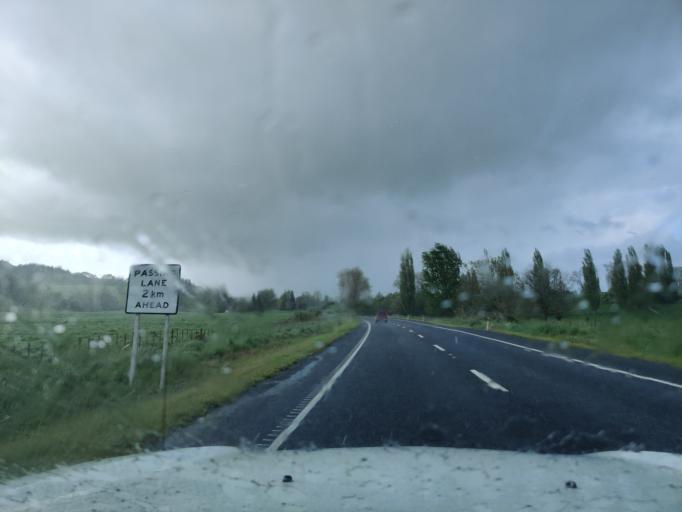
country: NZ
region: Waikato
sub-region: Matamata-Piako District
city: Matamata
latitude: -37.9754
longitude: 175.6960
